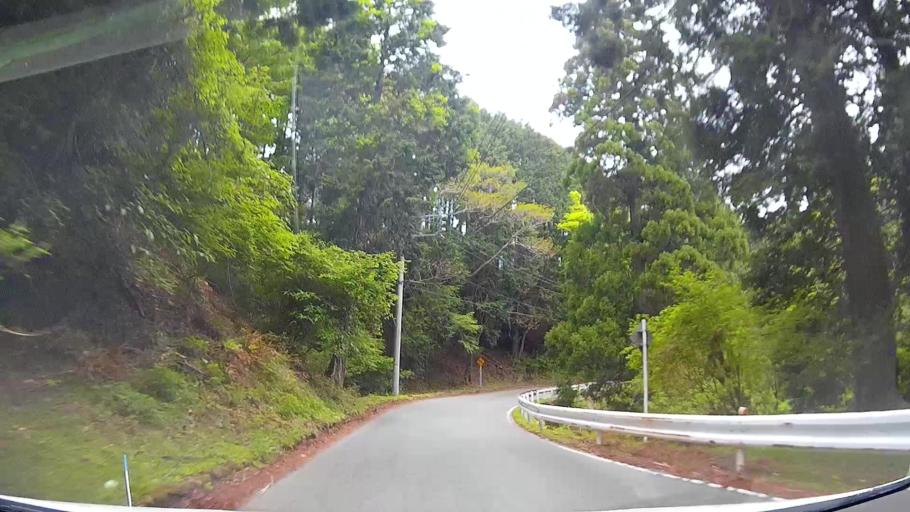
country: JP
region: Shizuoka
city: Ito
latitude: 34.9152
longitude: 139.0476
